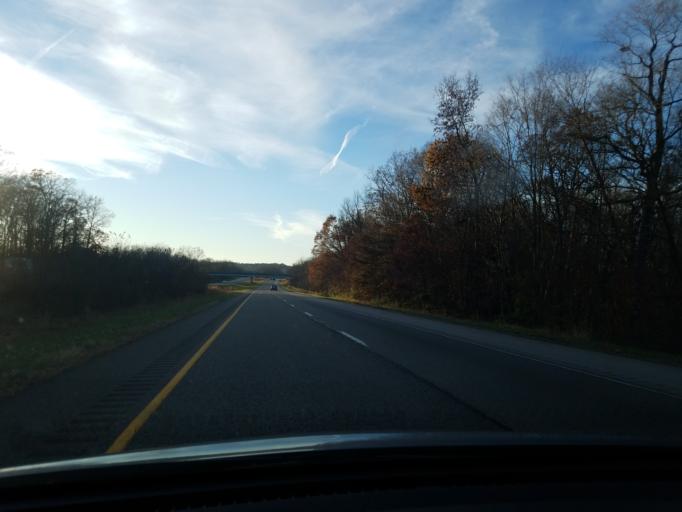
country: US
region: Indiana
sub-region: Spencer County
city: Dale
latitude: 38.1987
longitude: -87.1588
